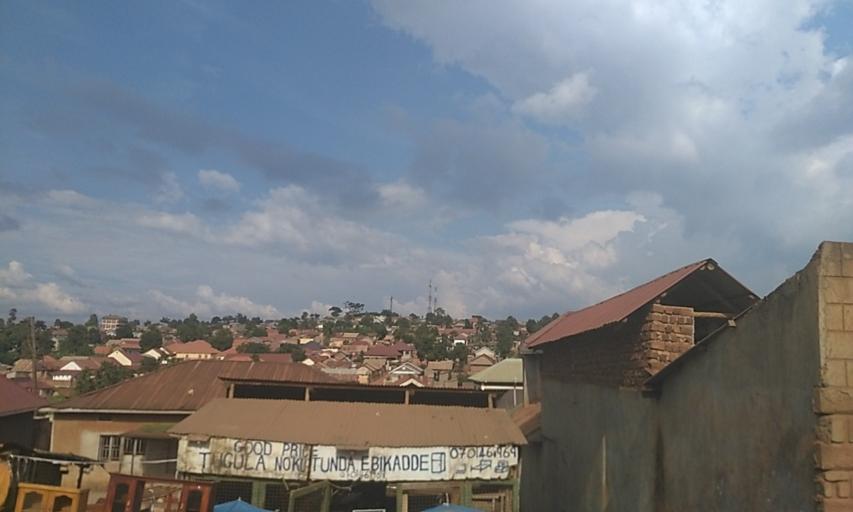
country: UG
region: Central Region
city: Kampala Central Division
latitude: 0.3383
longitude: 32.5471
